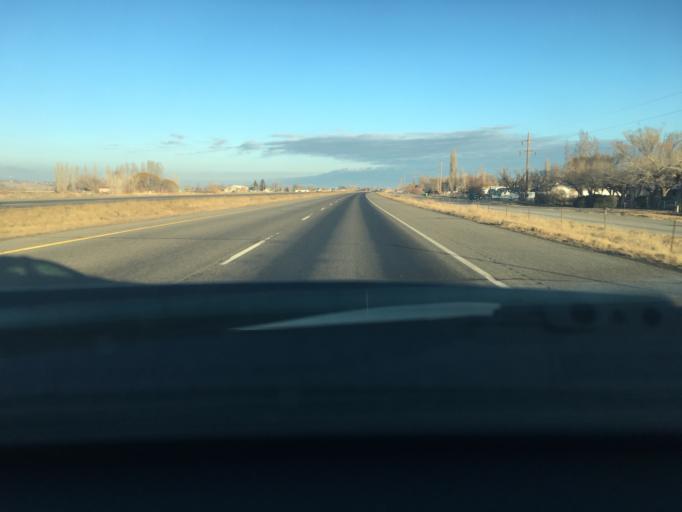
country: US
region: Colorado
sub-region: Montrose County
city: Olathe
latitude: 38.5519
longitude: -107.9494
